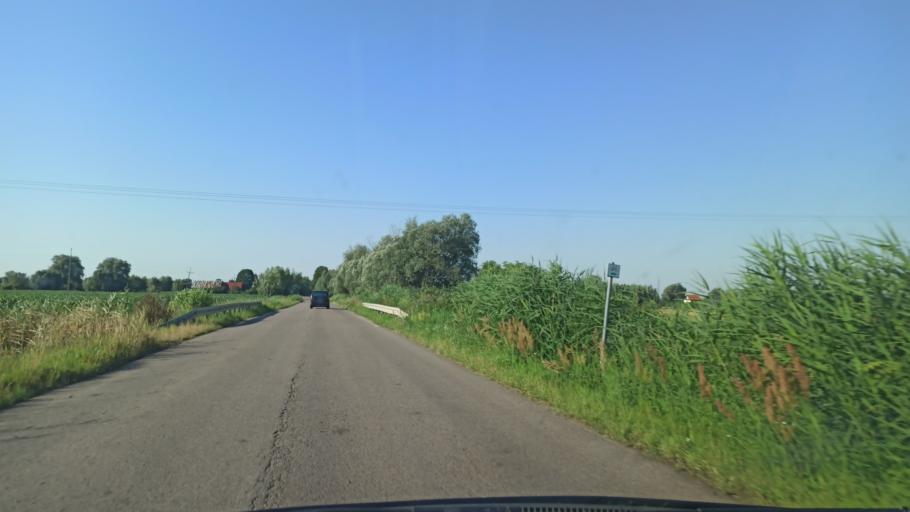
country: PL
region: Warmian-Masurian Voivodeship
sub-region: Powiat elblaski
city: Elblag
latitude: 54.1779
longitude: 19.3318
